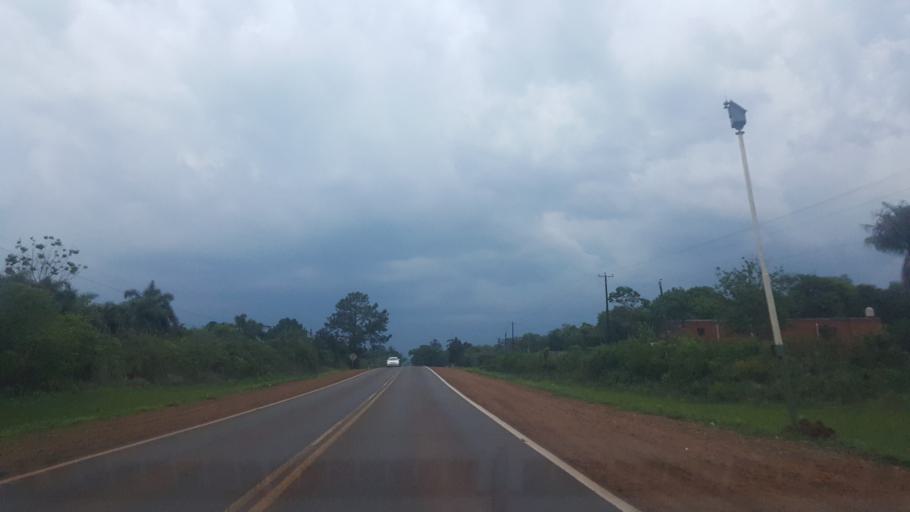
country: AR
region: Misiones
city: Gobernador Roca
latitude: -27.1750
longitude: -55.4518
